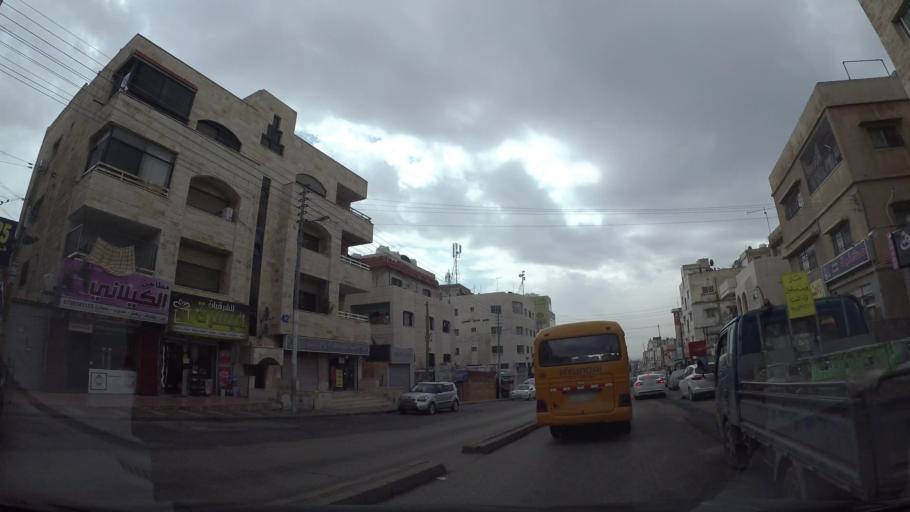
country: JO
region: Amman
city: Amman
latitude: 31.9830
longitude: 35.9242
